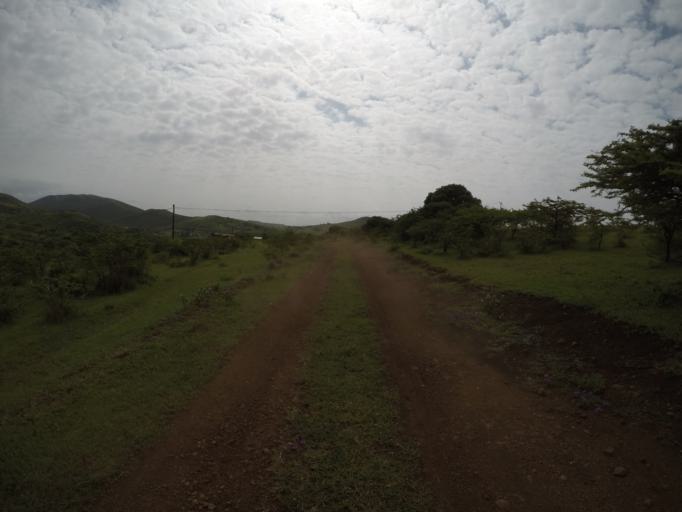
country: ZA
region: KwaZulu-Natal
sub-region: uThungulu District Municipality
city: Empangeni
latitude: -28.6227
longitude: 31.9083
